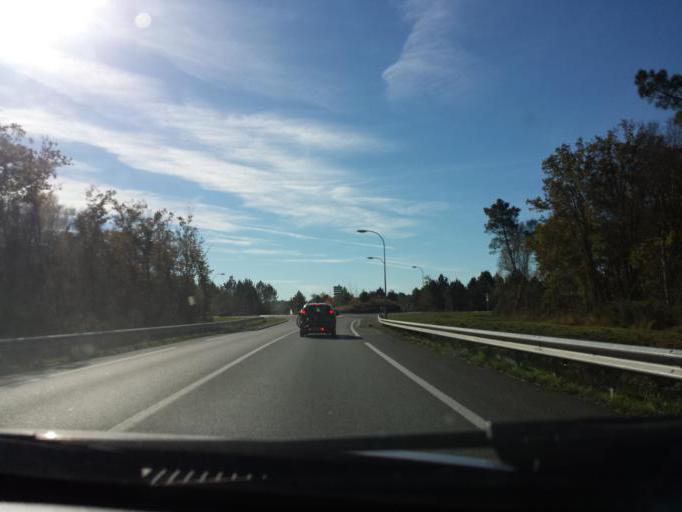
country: FR
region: Aquitaine
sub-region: Departement de la Gironde
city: Lacanau
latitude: 44.9775
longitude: -1.0618
